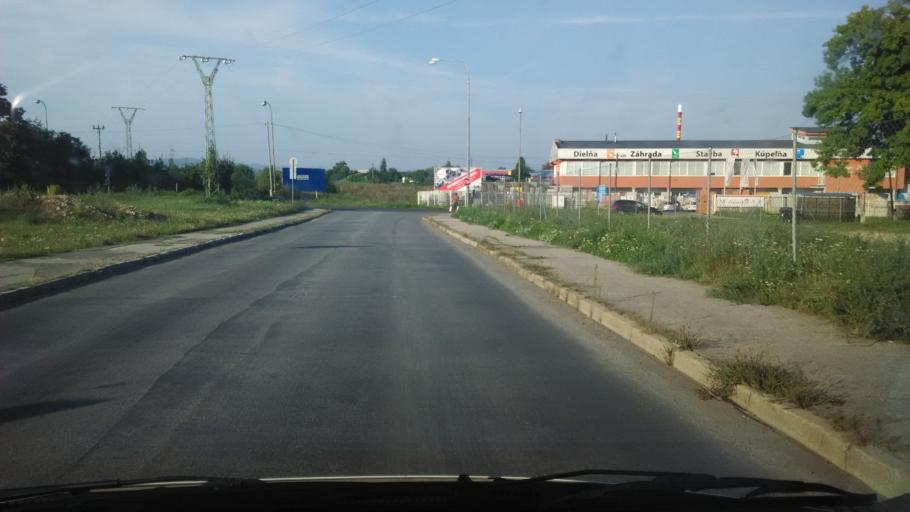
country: SK
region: Nitriansky
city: Levice
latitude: 48.2172
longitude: 18.6281
